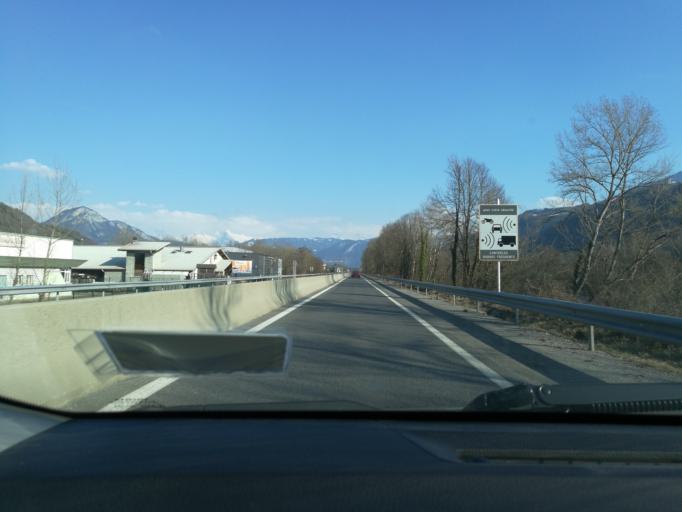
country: FR
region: Rhone-Alpes
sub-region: Departement de la Haute-Savoie
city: Ayse
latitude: 46.0745
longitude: 6.4483
